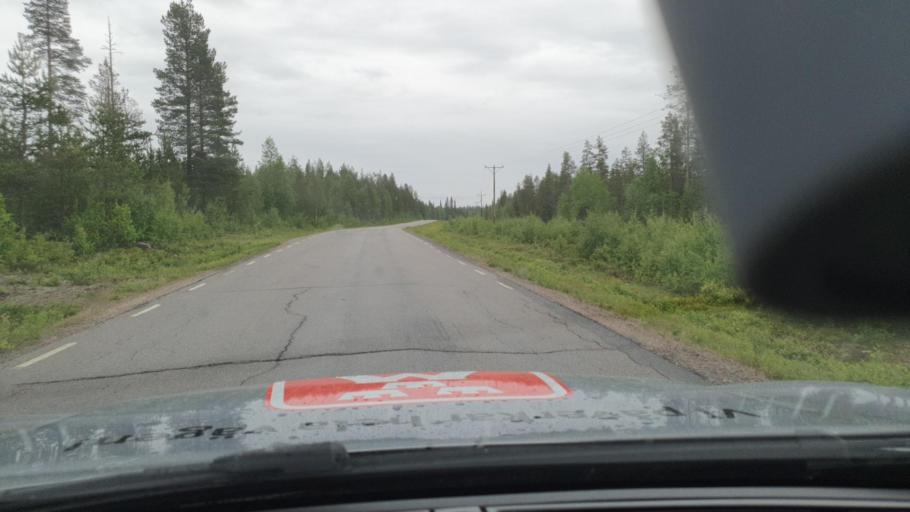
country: SE
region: Norrbotten
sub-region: Pajala Kommun
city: Pajala
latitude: 66.7809
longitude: 23.1368
